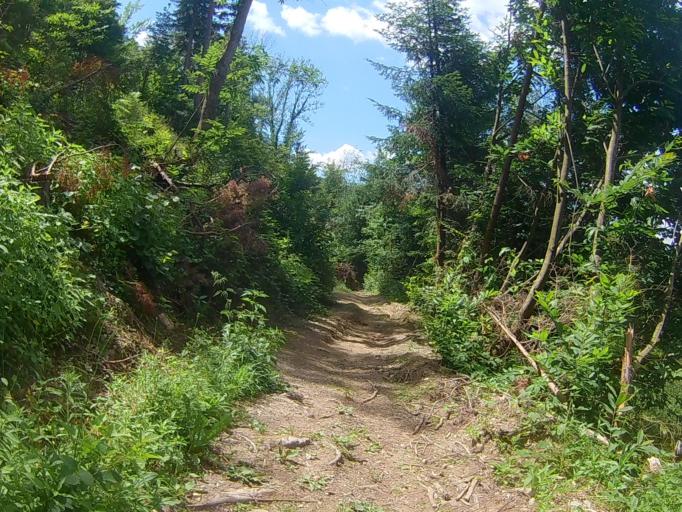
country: SI
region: Ruse
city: Ruse
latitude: 46.5354
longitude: 15.5099
